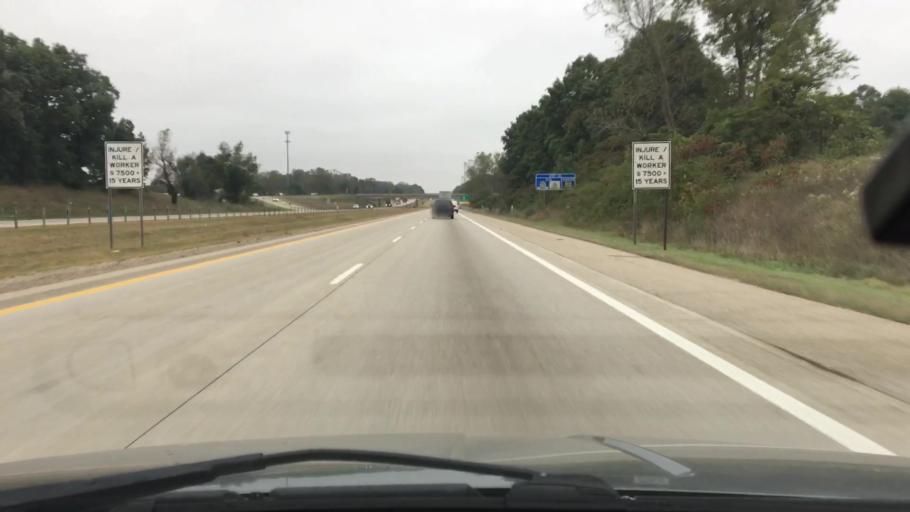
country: US
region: Michigan
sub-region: Van Buren County
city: Paw Paw
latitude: 42.2011
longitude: -85.9608
